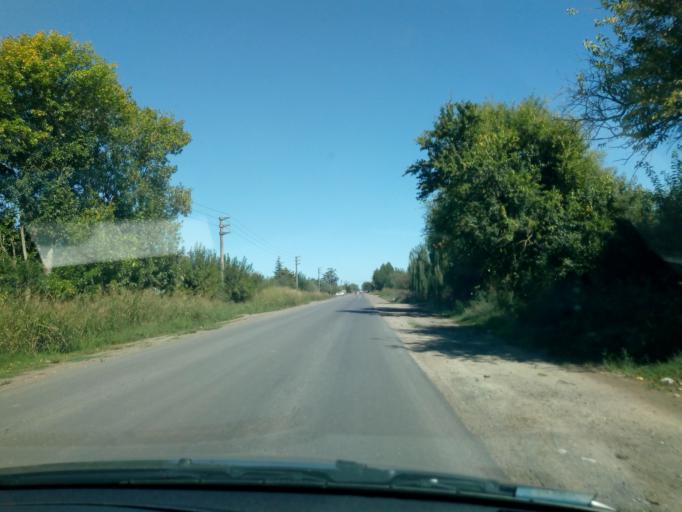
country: AR
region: Buenos Aires
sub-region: Partido de La Plata
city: La Plata
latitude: -35.0070
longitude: -58.0238
